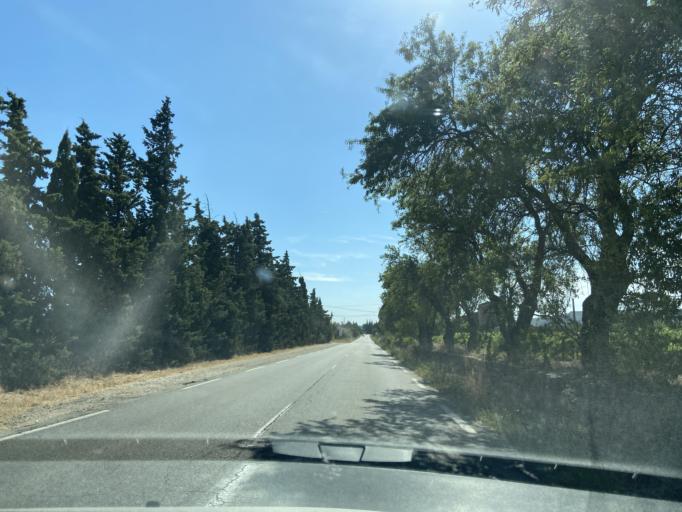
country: FR
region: Provence-Alpes-Cote d'Azur
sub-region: Departement des Bouches-du-Rhone
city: La Fare-les-Oliviers
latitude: 43.5484
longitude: 5.1698
